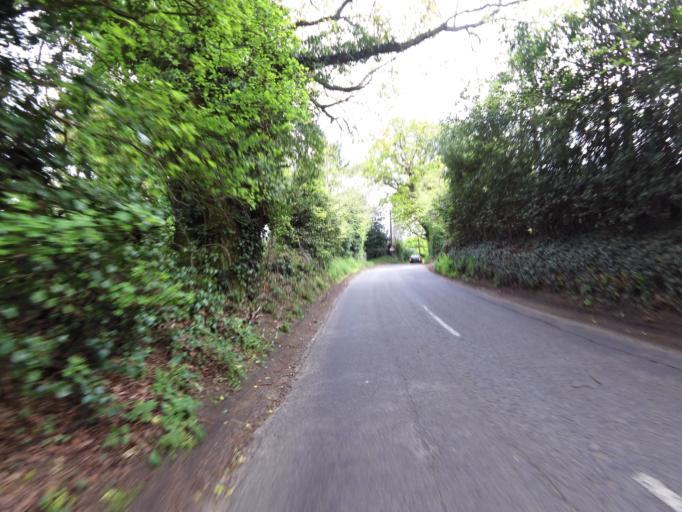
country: GB
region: England
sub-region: Suffolk
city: Ipswich
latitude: 51.9750
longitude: 1.1680
